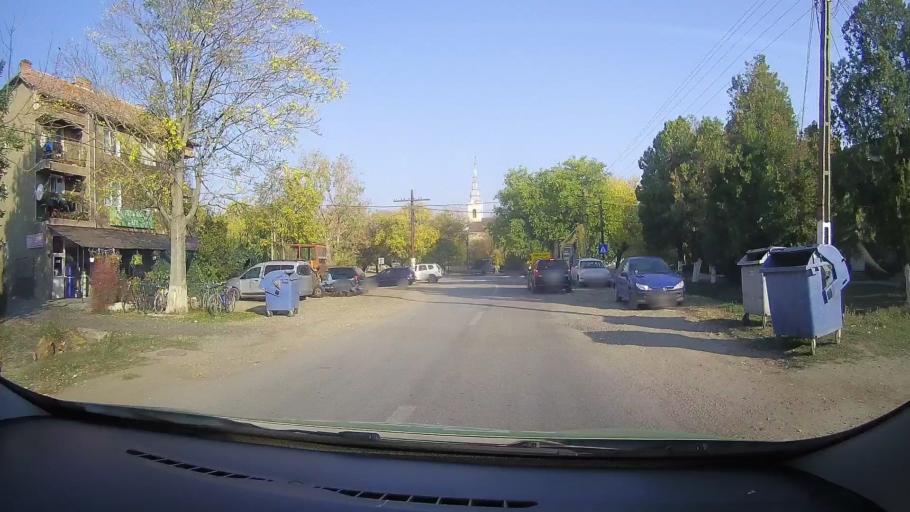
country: RO
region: Arad
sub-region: Comuna Graniceri
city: Graniceri
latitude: 46.5180
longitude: 21.3041
